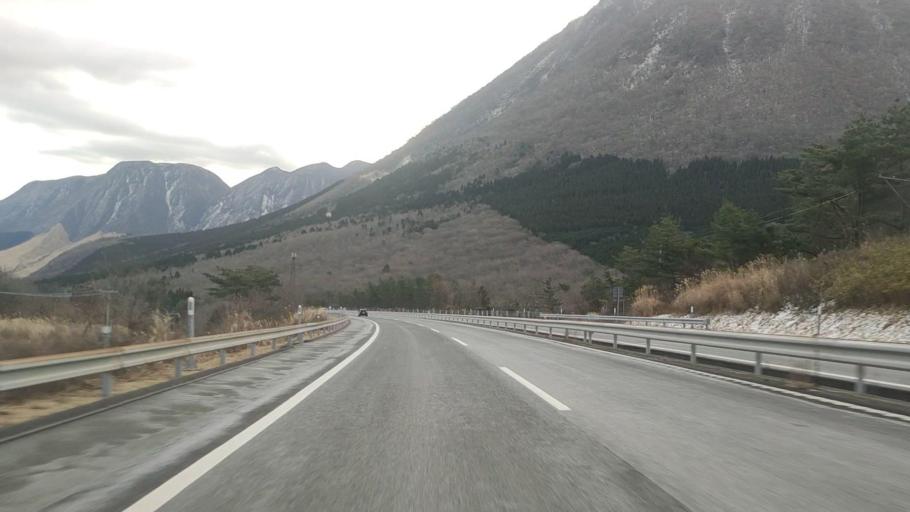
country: JP
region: Oita
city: Beppu
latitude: 33.2953
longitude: 131.3698
